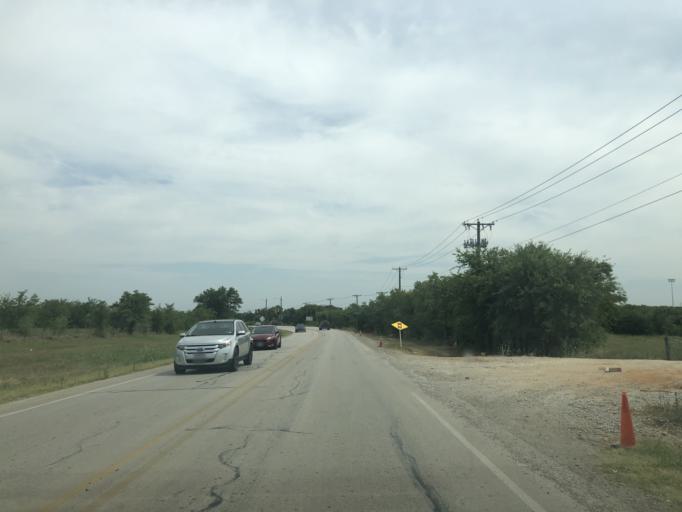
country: US
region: Texas
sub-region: Tarrant County
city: Saginaw
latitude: 32.8966
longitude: -97.3490
